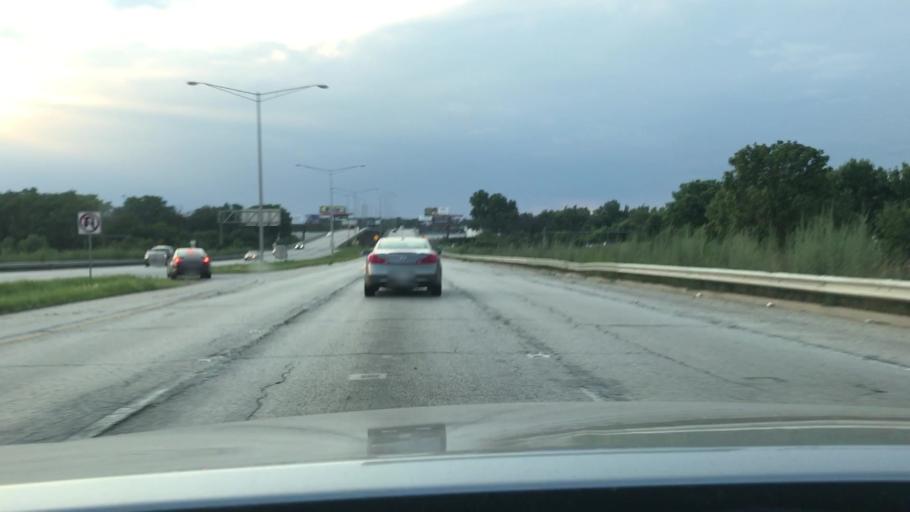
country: US
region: Illinois
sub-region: Cook County
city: Willow Springs
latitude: 41.7514
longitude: -87.8594
